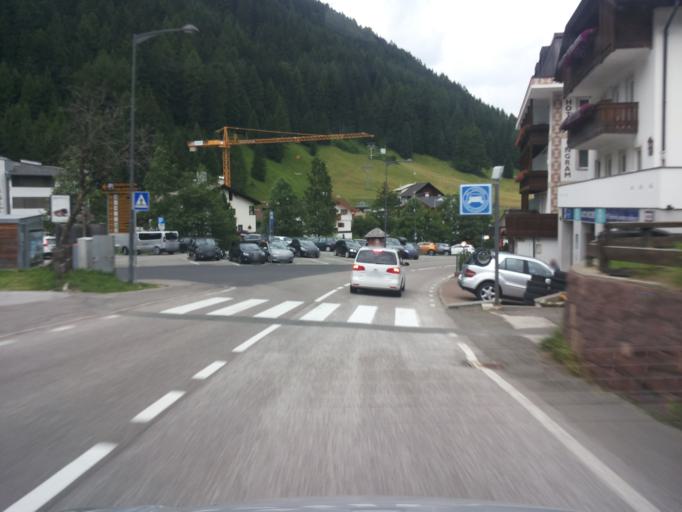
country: IT
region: Trentino-Alto Adige
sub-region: Bolzano
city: Selva
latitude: 46.5462
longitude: 11.7694
